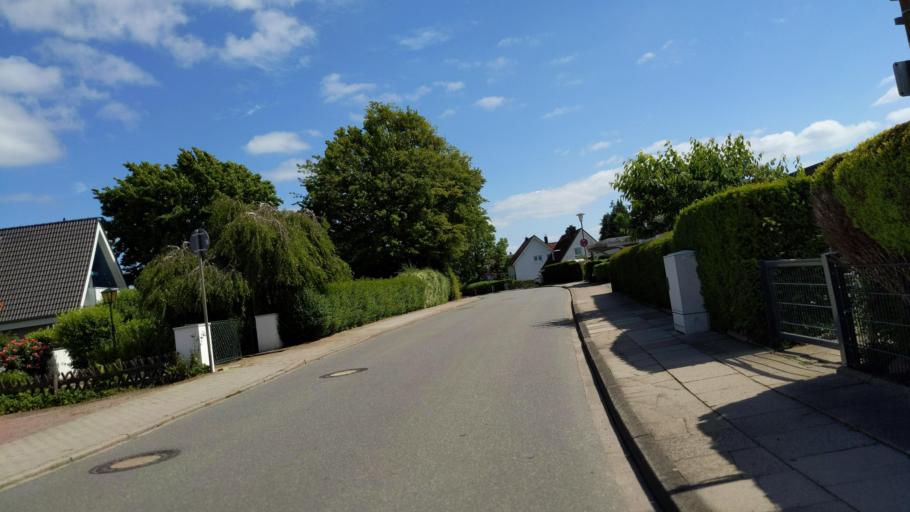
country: DE
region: Schleswig-Holstein
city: Scharbeutz
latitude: 54.0185
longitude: 10.7524
